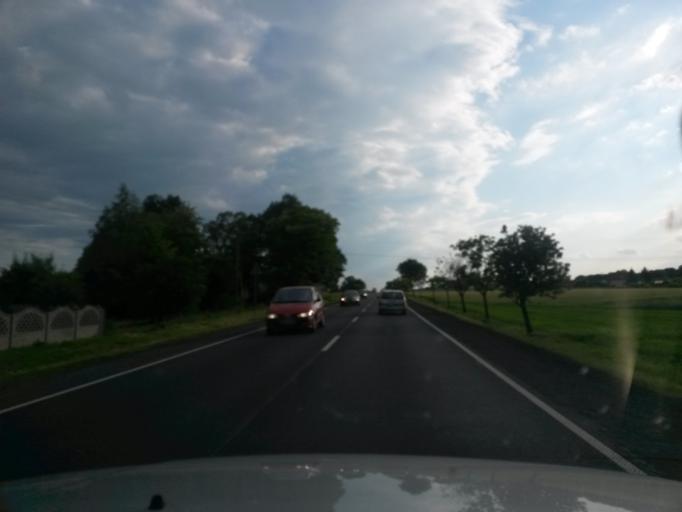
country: PL
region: Lodz Voivodeship
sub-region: Powiat belchatowski
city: Druzbice
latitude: 51.4130
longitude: 19.4655
